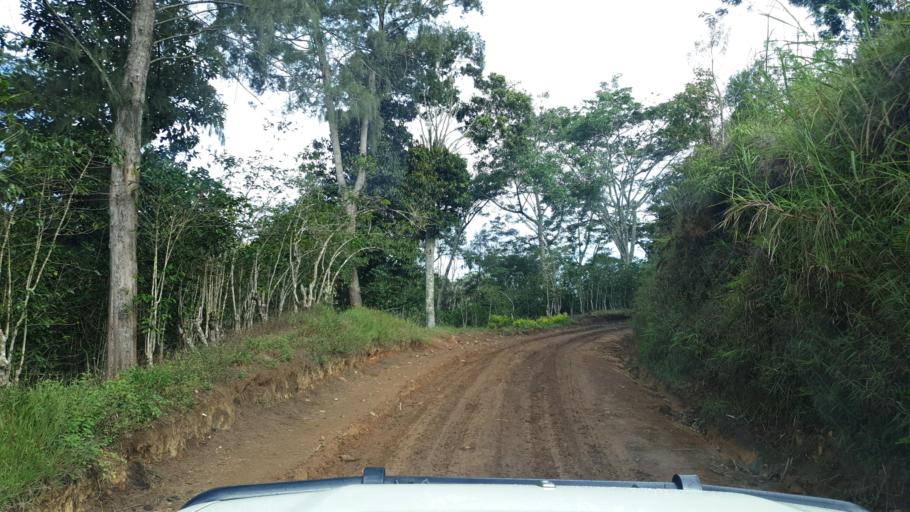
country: PG
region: Eastern Highlands
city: Goroka
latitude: -5.9217
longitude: 145.2641
